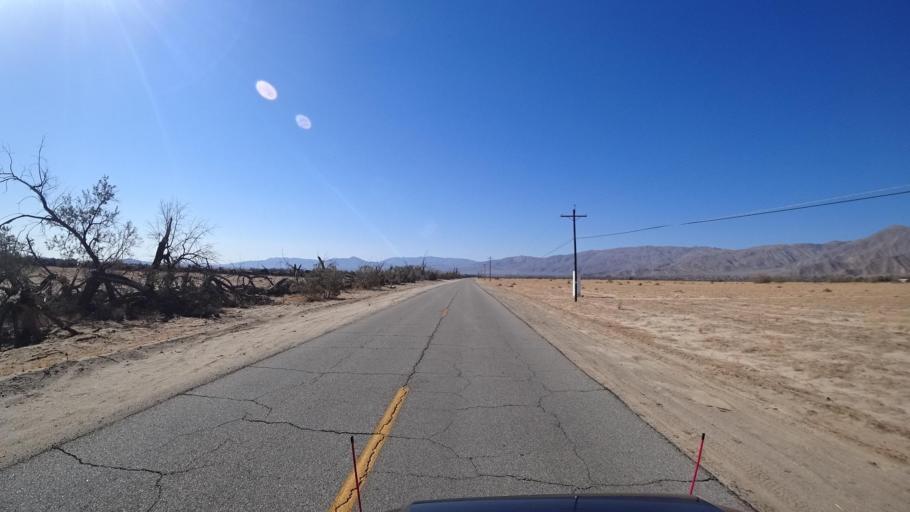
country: US
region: California
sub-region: San Diego County
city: Borrego Springs
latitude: 33.2993
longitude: -116.3667
